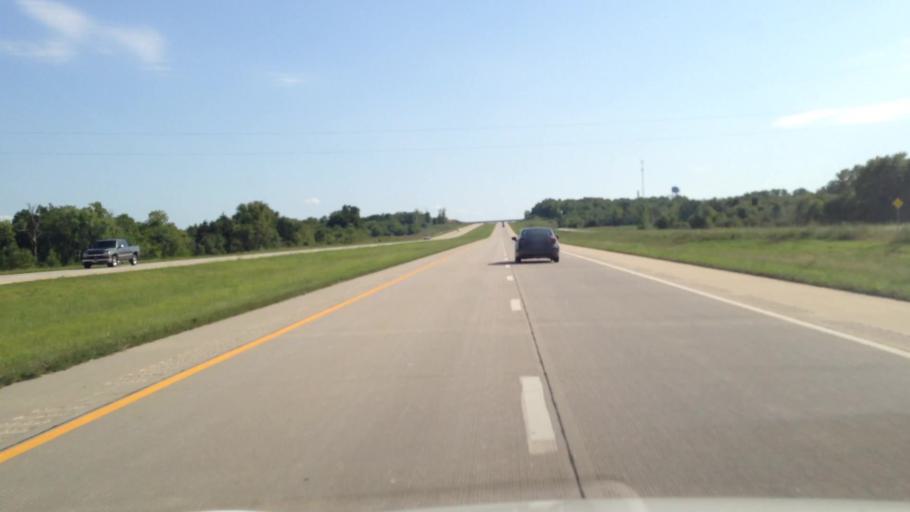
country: US
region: Kansas
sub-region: Linn County
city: Pleasanton
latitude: 38.1261
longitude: -94.7150
